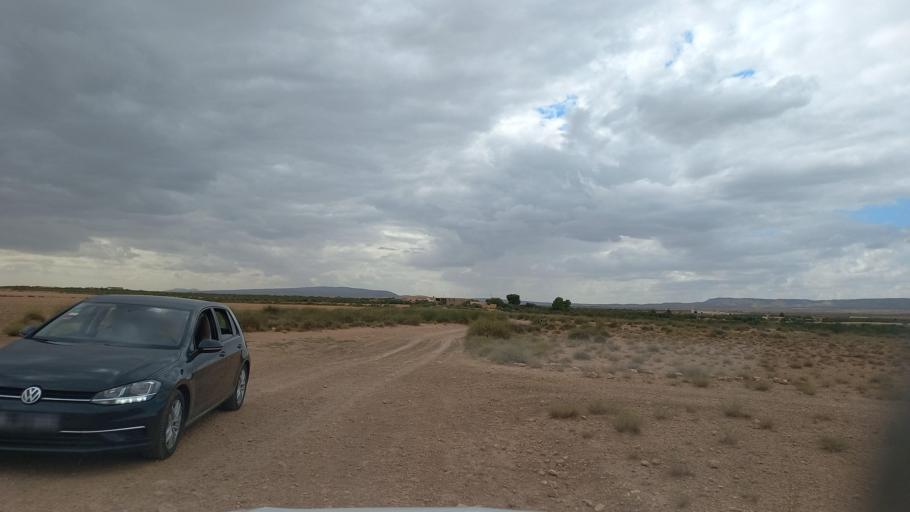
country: TN
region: Al Qasrayn
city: Sbiba
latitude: 35.3958
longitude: 9.1045
